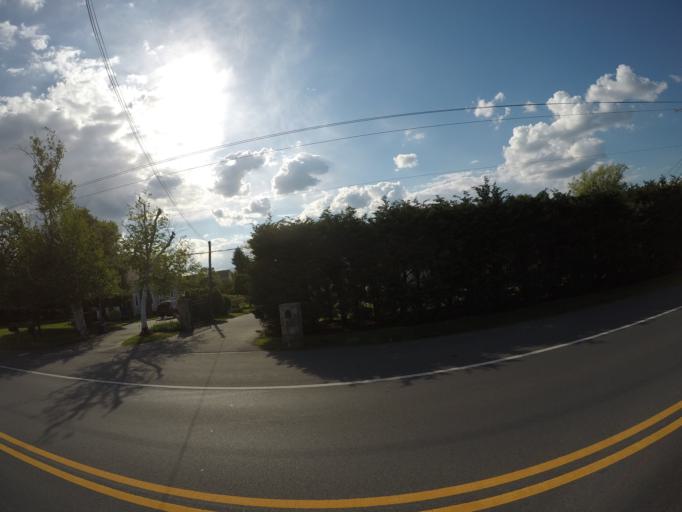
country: US
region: Maryland
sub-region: Montgomery County
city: Clarksburg
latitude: 39.2346
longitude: -77.2350
